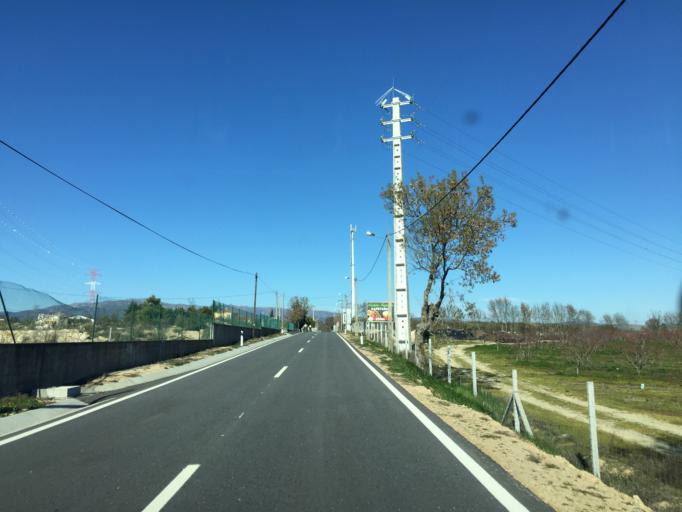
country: PT
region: Guarda
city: Alcains
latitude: 39.9799
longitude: -7.4570
